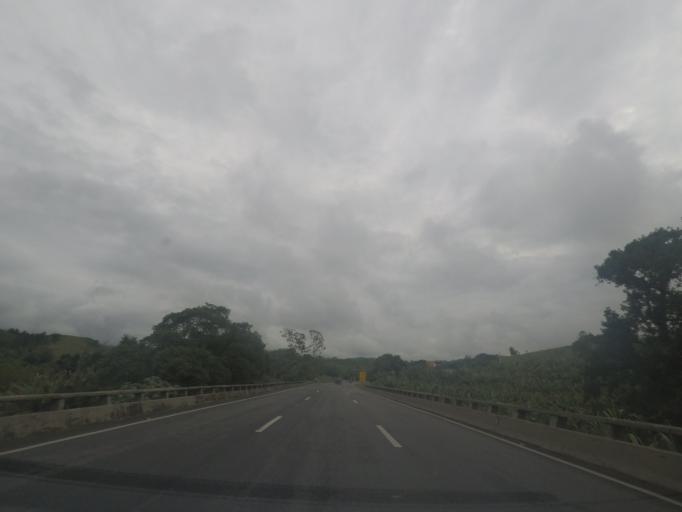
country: BR
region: Sao Paulo
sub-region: Cajati
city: Cajati
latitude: -24.7779
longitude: -48.1726
